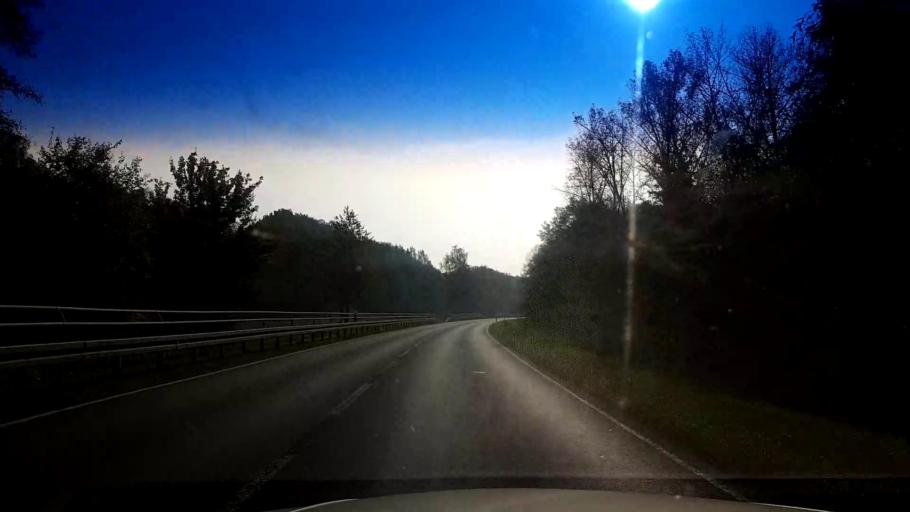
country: DE
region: Bavaria
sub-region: Upper Franconia
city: Neuenmarkt
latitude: 50.1119
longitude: 11.5872
